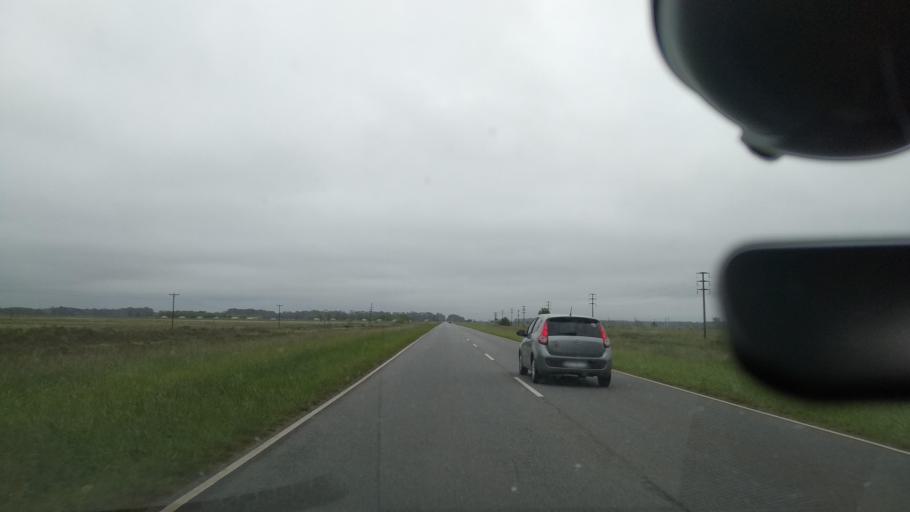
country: AR
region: Buenos Aires
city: Veronica
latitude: -35.3354
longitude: -57.4573
